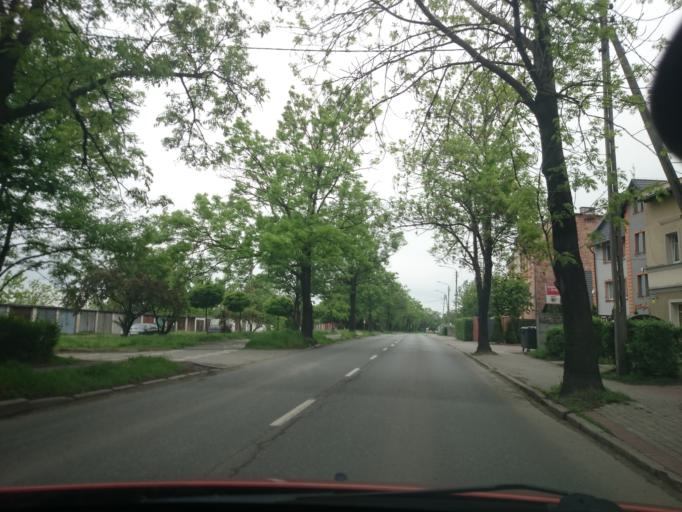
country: PL
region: Opole Voivodeship
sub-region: Powiat opolski
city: Opole
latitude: 50.6775
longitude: 17.9233
